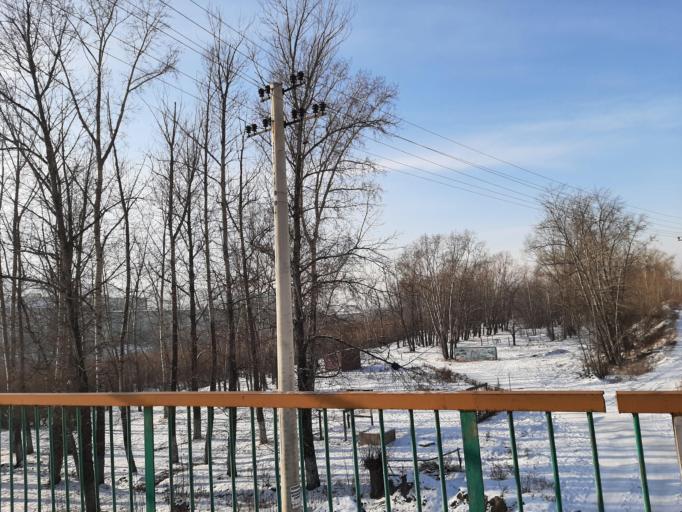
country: RU
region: Transbaikal Territory
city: Chita
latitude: 52.0269
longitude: 113.4950
